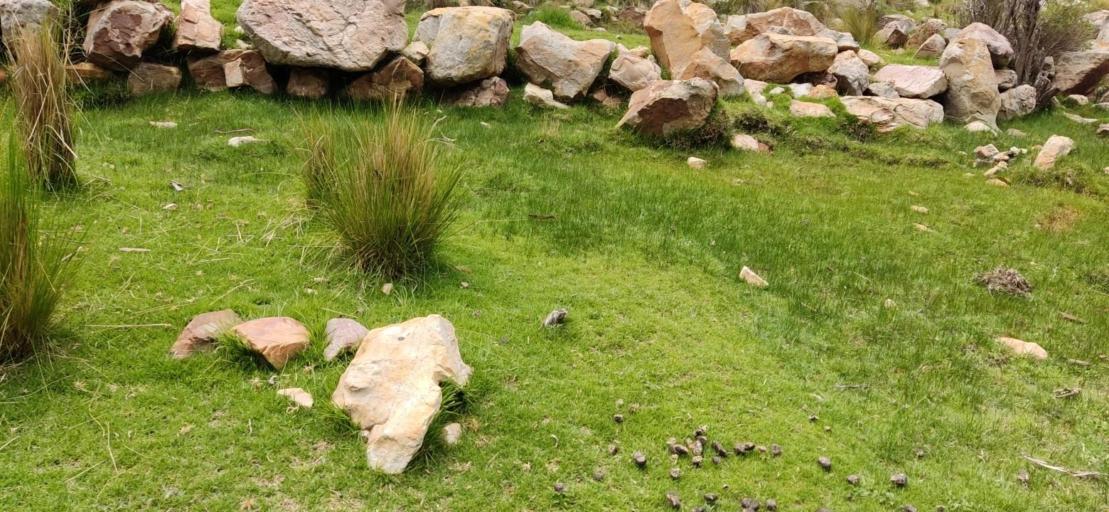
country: BO
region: La Paz
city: Batallas
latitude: -16.3469
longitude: -68.6416
